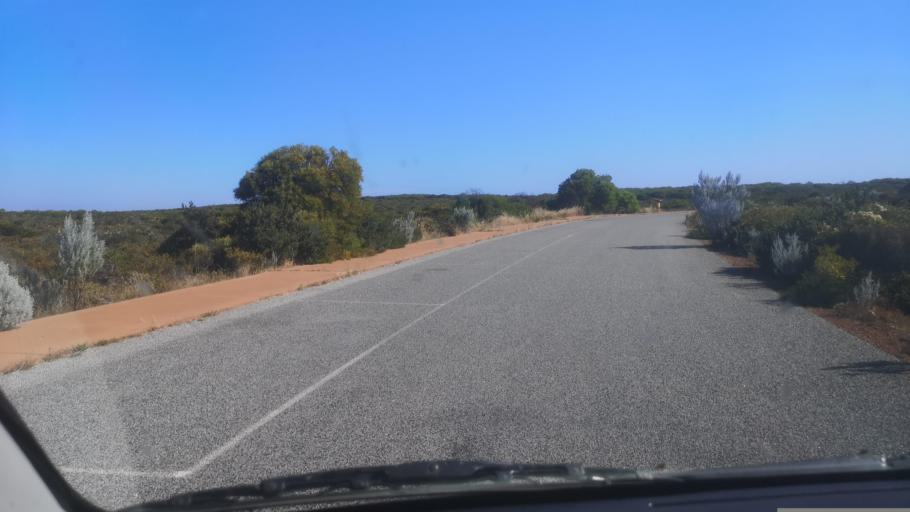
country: AU
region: Western Australia
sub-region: Dandaragan
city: Jurien Bay
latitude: -30.7910
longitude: 115.2260
